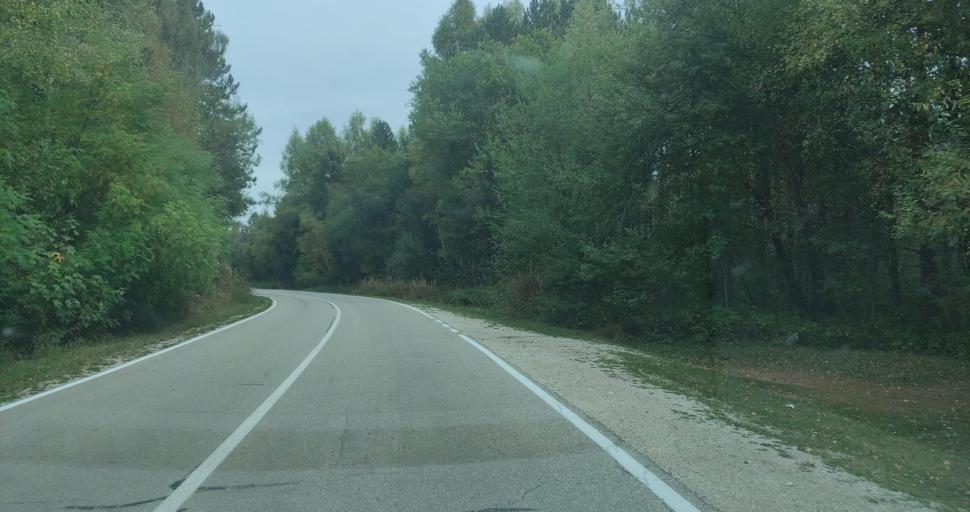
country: RS
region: Central Serbia
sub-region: Jablanicki Okrug
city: Crna Trava
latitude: 42.7250
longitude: 22.3359
